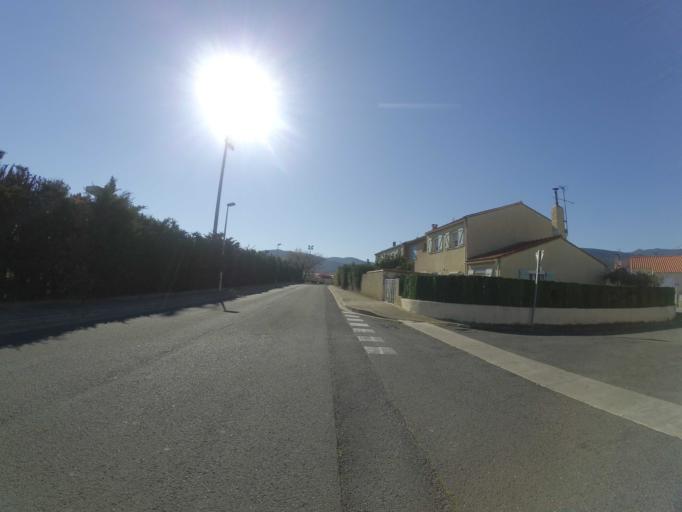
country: FR
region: Languedoc-Roussillon
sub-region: Departement des Pyrenees-Orientales
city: Ille-sur-Tet
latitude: 42.6668
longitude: 2.6148
